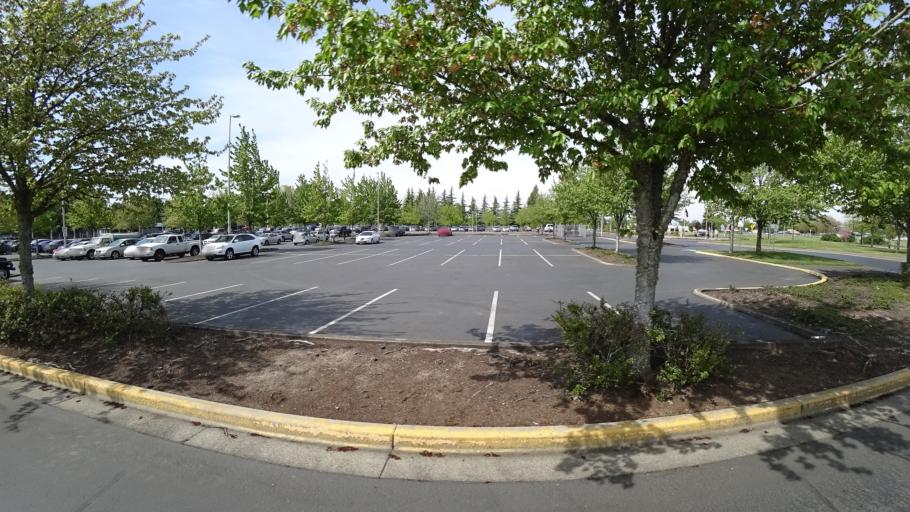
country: US
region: Oregon
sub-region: Washington County
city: Hillsboro
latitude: 45.5281
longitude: -122.9454
